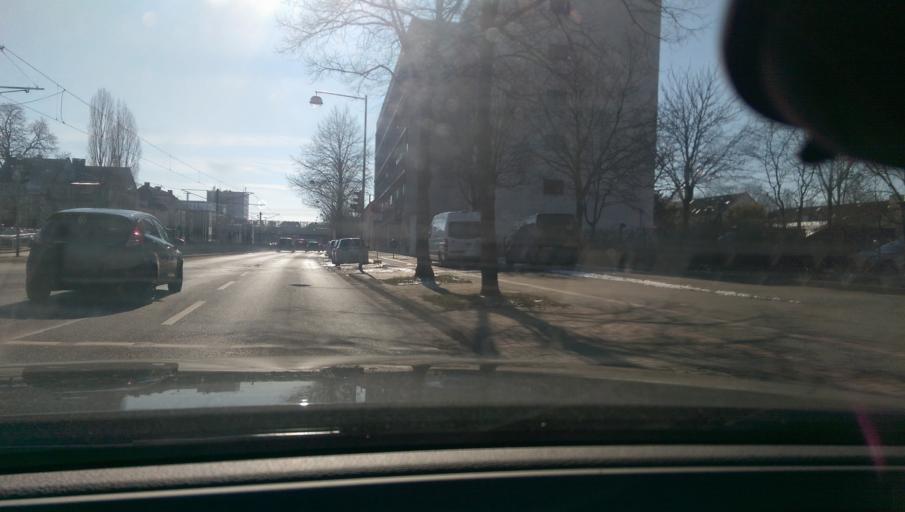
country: DE
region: Lower Saxony
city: Hannover
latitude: 52.3459
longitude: 9.7615
